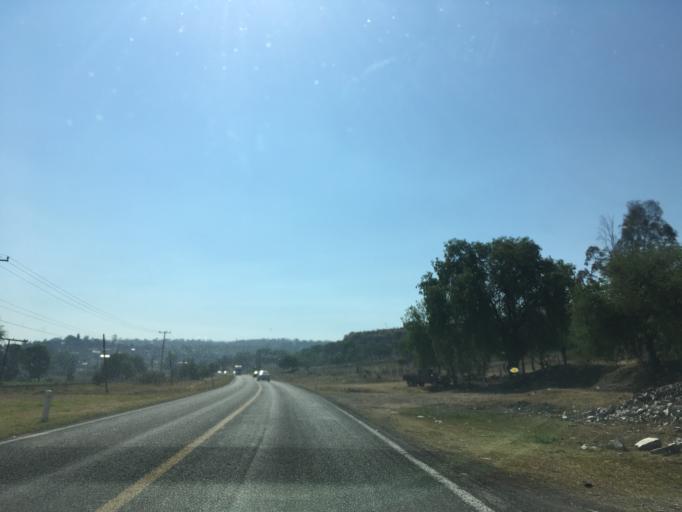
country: MX
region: Michoacan
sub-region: Morelia
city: Fraccionamiento Mision del Valle
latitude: 19.7358
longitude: -101.0903
